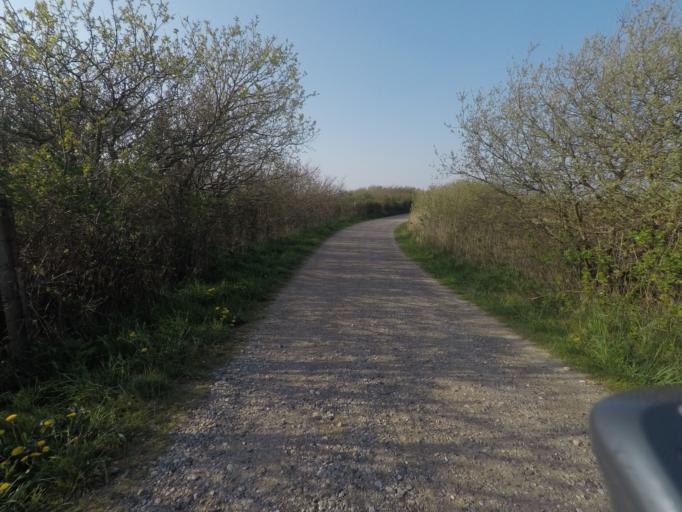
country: DE
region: Schleswig-Holstein
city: List
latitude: 55.1473
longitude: 8.4982
